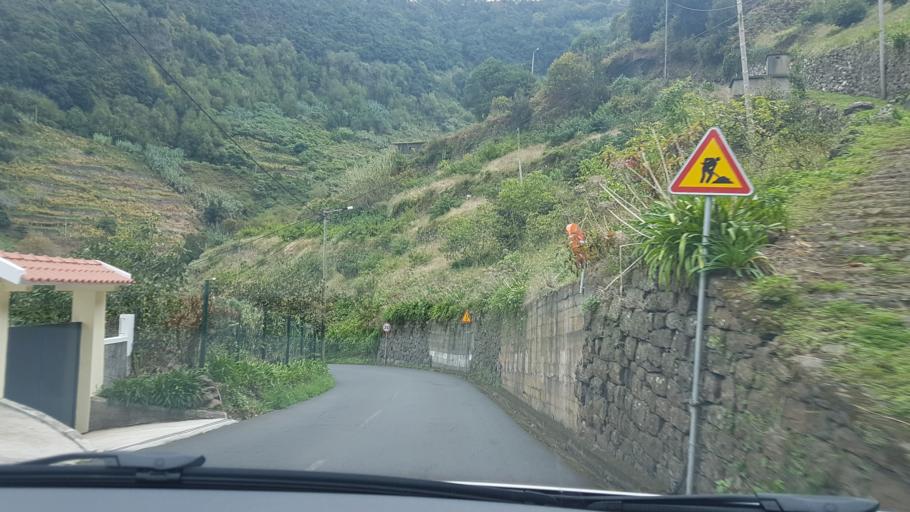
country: PT
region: Madeira
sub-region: Santana
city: Santana
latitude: 32.8185
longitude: -16.9007
